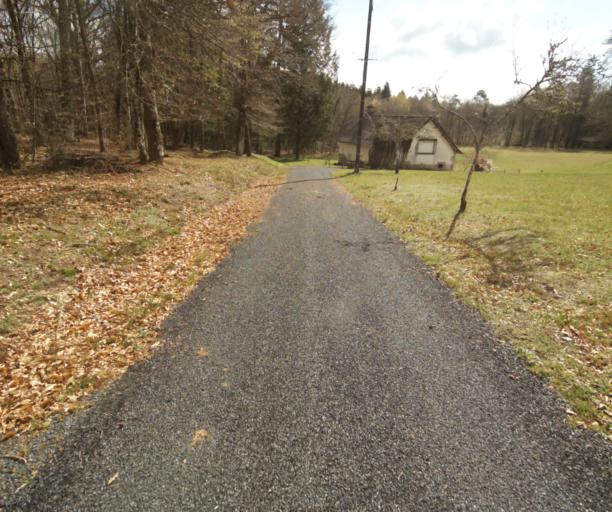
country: FR
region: Limousin
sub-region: Departement de la Correze
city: Argentat
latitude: 45.2245
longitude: 1.9360
